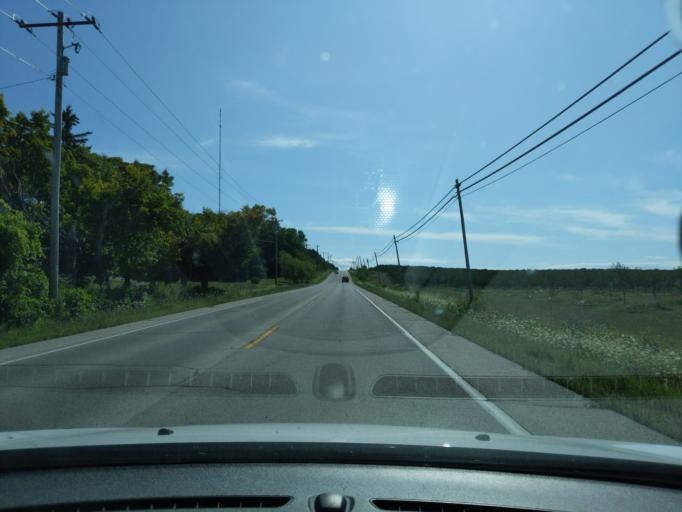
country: US
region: Wisconsin
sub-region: Door County
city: Sturgeon Bay
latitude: 45.2423
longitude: -87.0887
